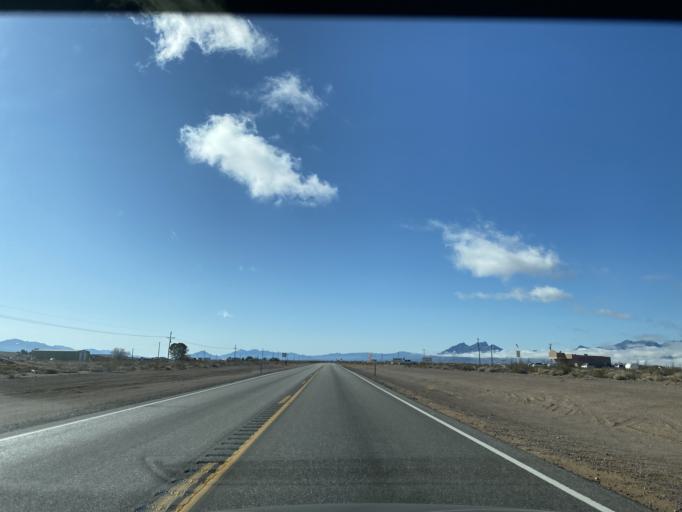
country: US
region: Nevada
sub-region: Nye County
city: Beatty
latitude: 36.5312
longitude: -116.4186
